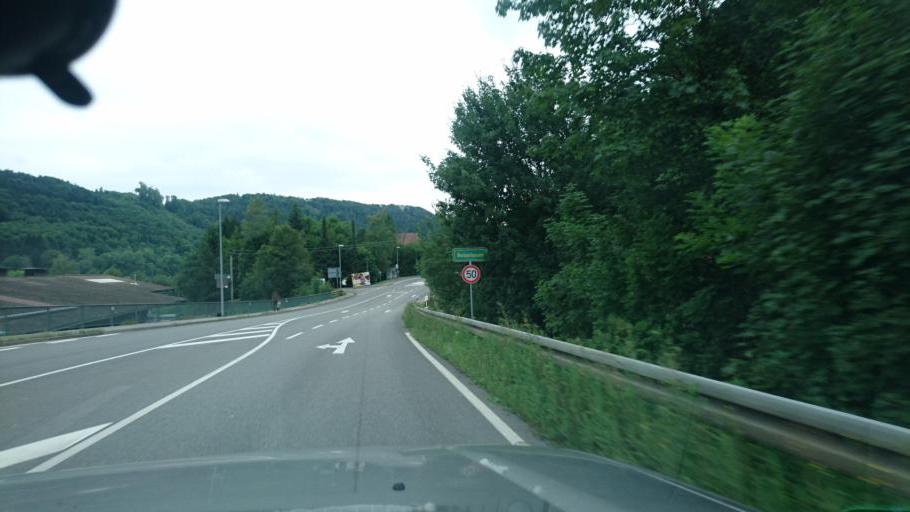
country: DE
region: Baden-Wuerttemberg
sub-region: Freiburg Region
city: Sulz am Neckar
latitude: 48.3981
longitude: 8.6486
